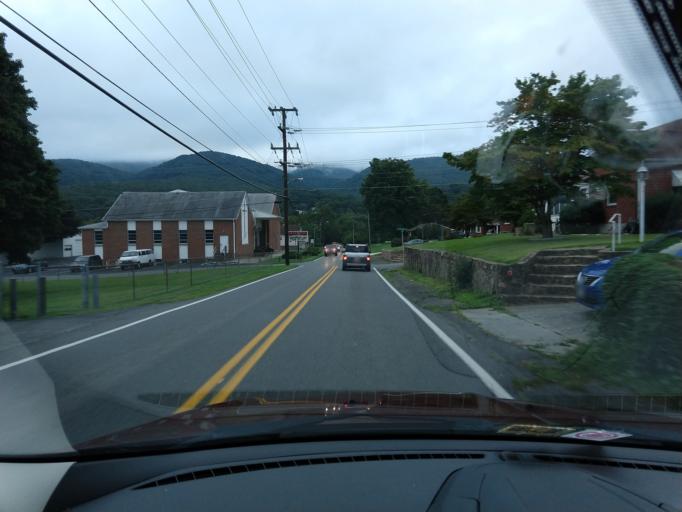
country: US
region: Virginia
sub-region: City of Covington
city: Fairlawn
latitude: 37.7594
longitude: -79.9879
